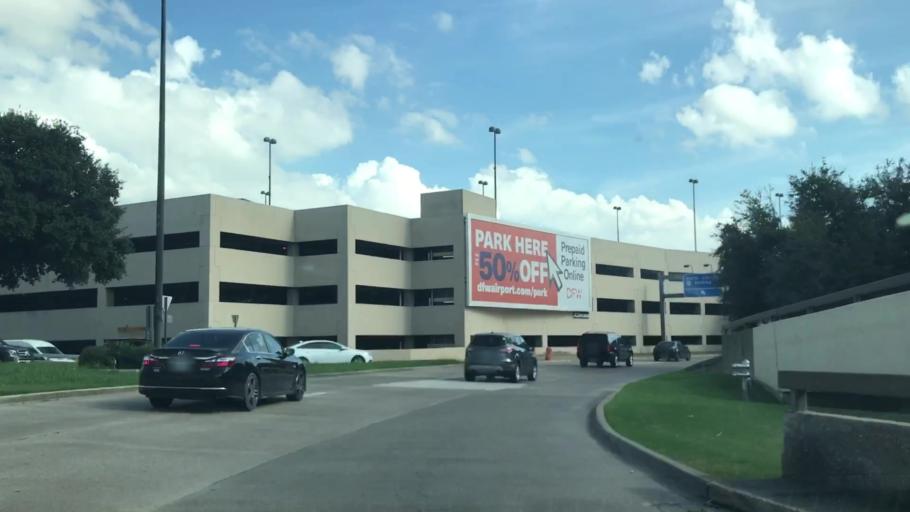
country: US
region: Texas
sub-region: Tarrant County
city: Grapevine
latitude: 32.8983
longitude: -97.0377
